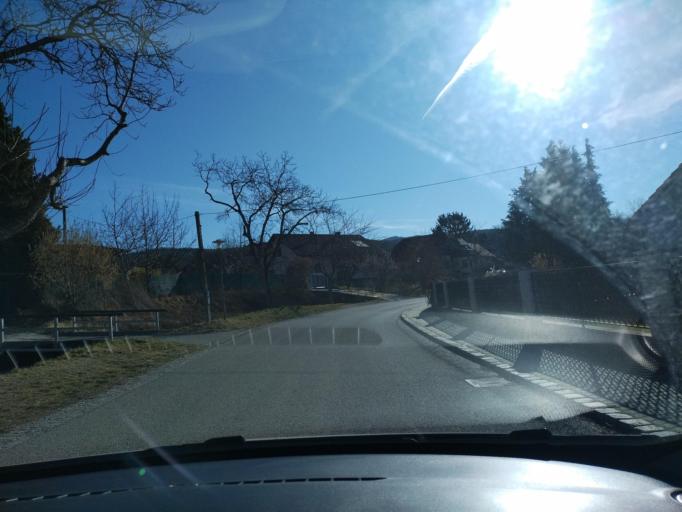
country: AT
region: Lower Austria
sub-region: Politischer Bezirk Wiener Neustadt
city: Lanzenkirchen
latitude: 47.7372
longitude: 16.2516
